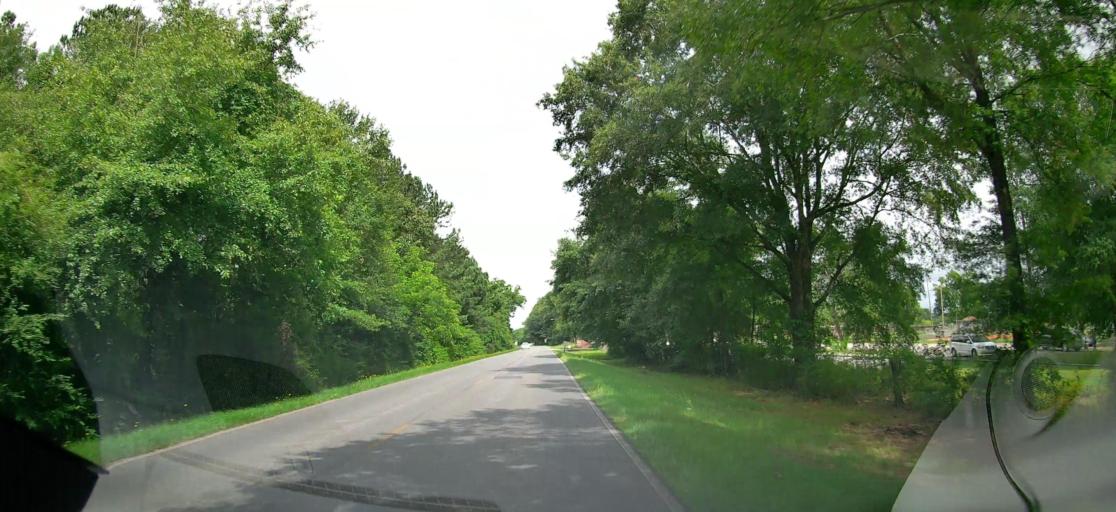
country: US
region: Georgia
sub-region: Peach County
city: Byron
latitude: 32.6452
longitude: -83.7489
